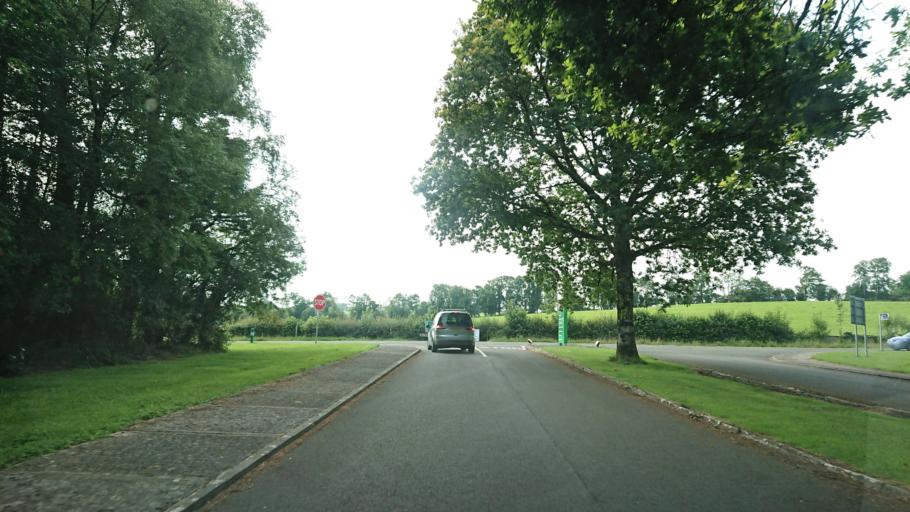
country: IE
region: Connaught
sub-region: Roscommon
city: Boyle
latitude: 53.9704
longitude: -8.2456
